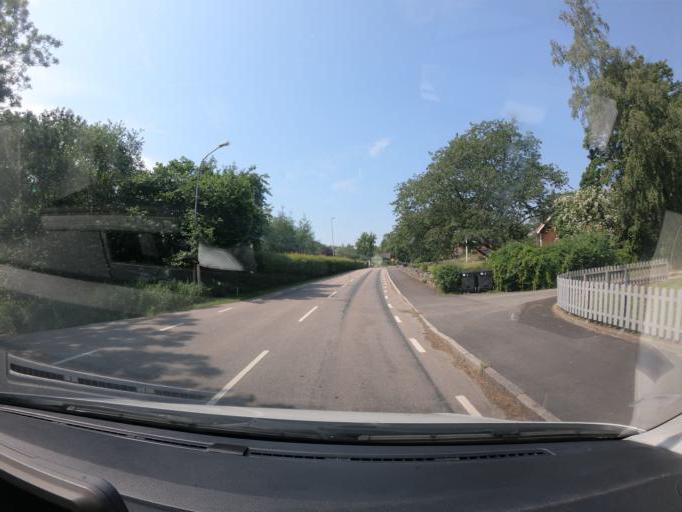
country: SE
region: Skane
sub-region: Hassleholms Kommun
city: Tormestorp
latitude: 56.1576
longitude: 13.6815
